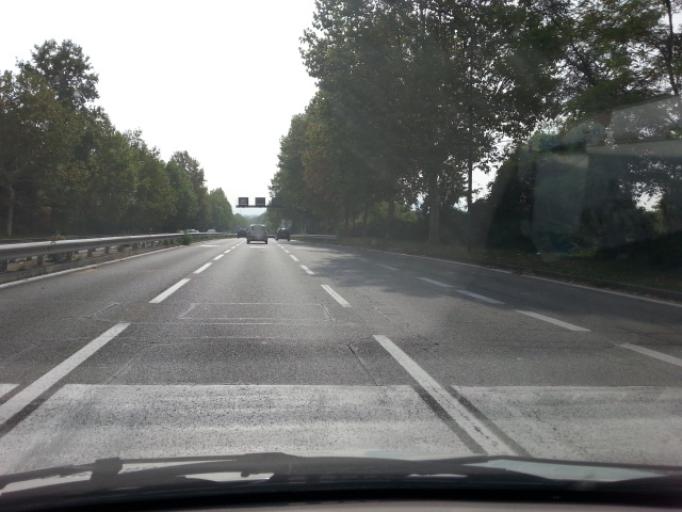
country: IT
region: Piedmont
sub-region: Provincia di Torino
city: Savonera
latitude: 45.0963
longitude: 7.6256
